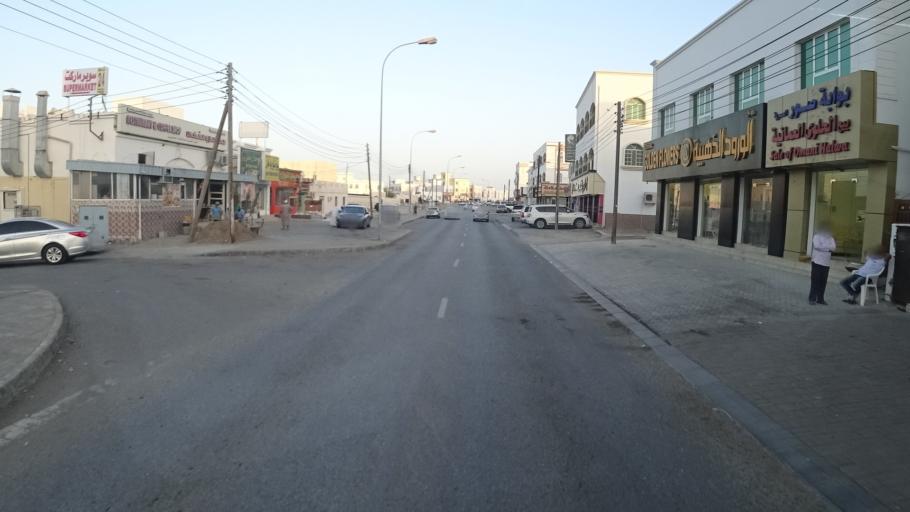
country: OM
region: Ash Sharqiyah
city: Sur
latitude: 22.5807
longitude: 59.5094
